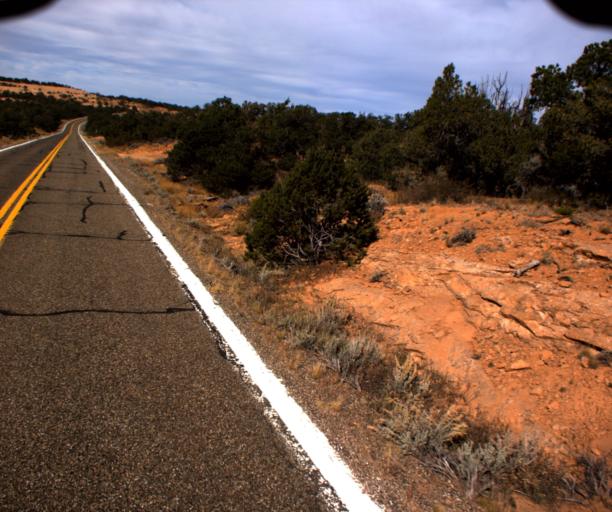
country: US
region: Arizona
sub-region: Navajo County
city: Kayenta
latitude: 36.6691
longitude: -110.5325
